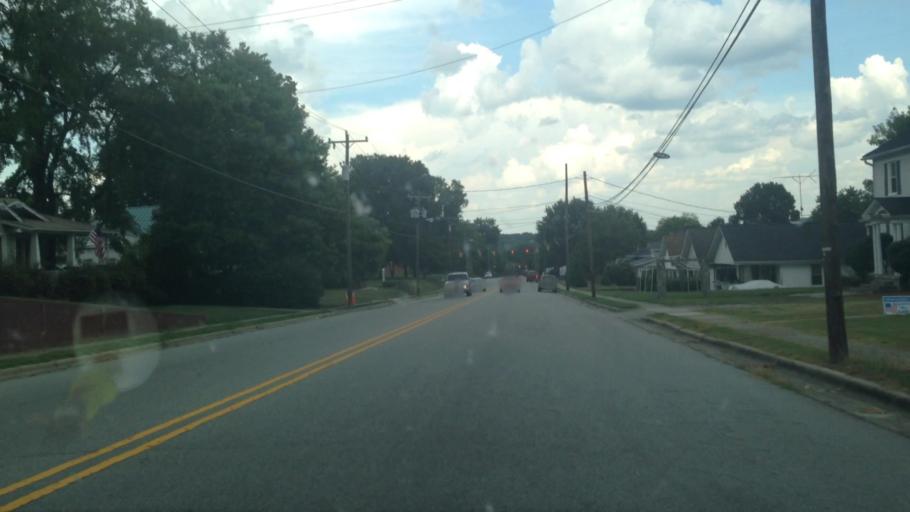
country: US
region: North Carolina
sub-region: Rockingham County
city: Madison
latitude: 36.3886
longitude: -79.9637
